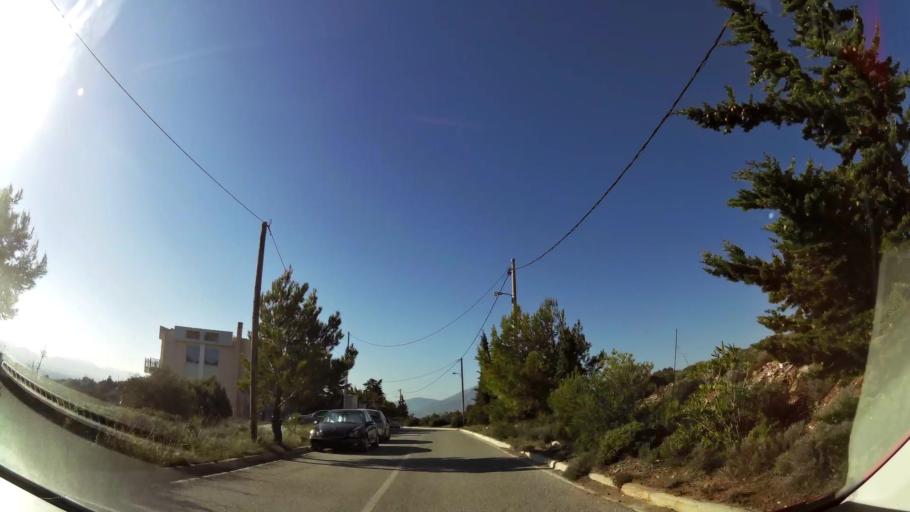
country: GR
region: Attica
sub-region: Nomarchia Anatolikis Attikis
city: Dhrafi
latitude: 38.0358
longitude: 23.8927
